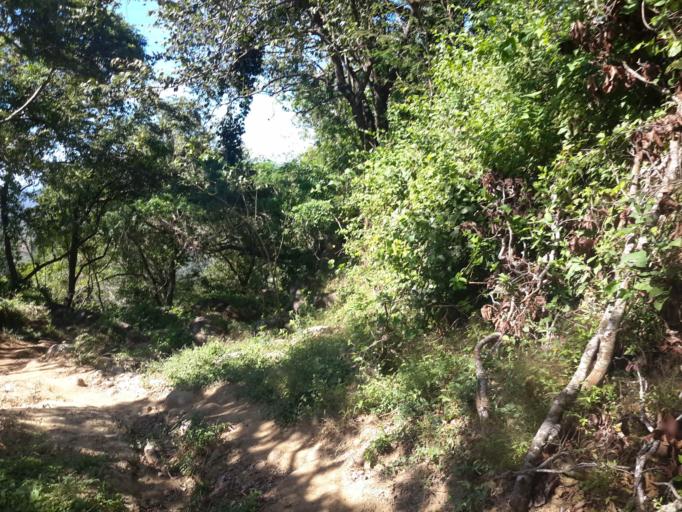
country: NI
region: Carazo
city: Santa Teresa
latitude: 11.6638
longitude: -86.1638
